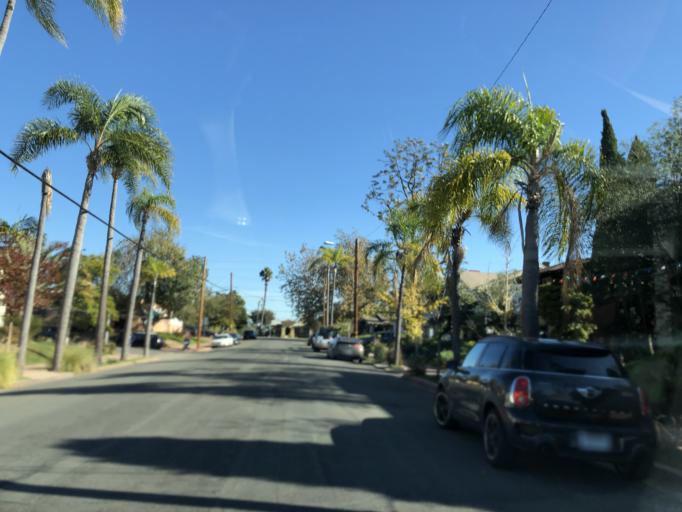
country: US
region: California
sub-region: San Diego County
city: San Diego
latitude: 32.7305
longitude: -117.1266
